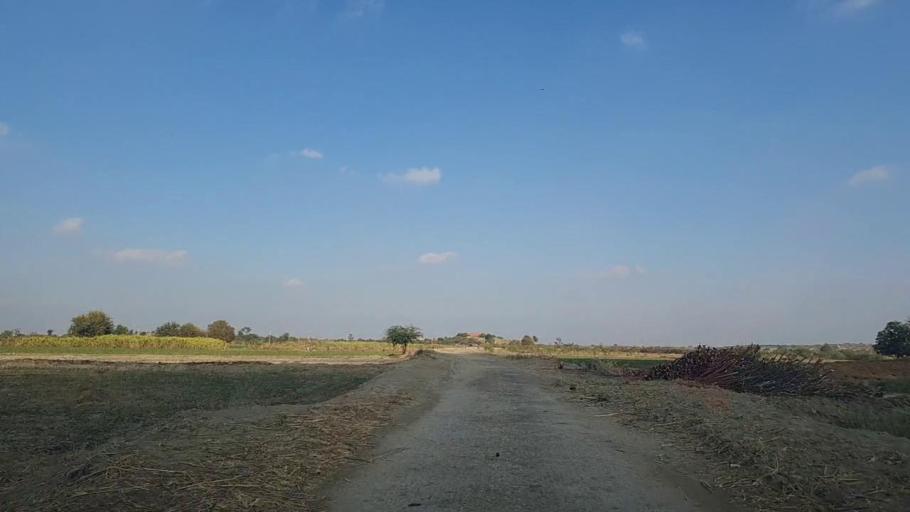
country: PK
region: Sindh
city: Tando Mittha Khan
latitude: 26.0004
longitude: 69.2546
